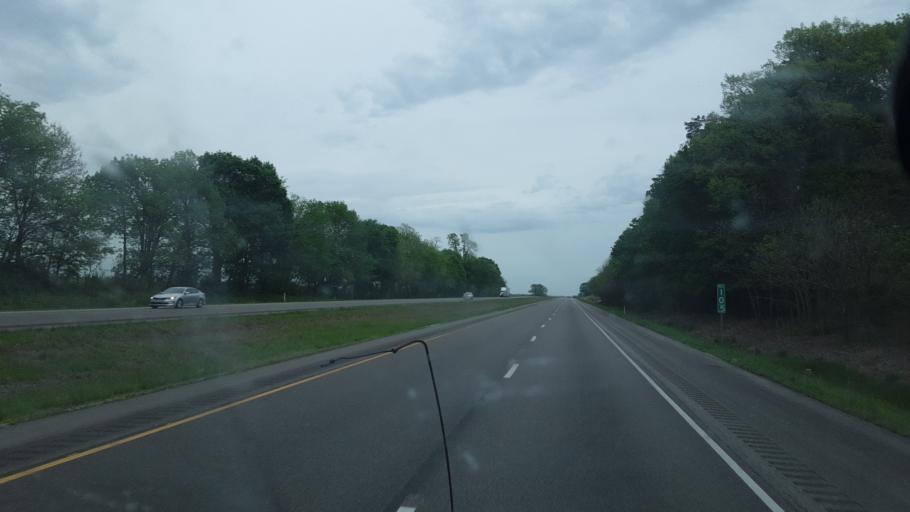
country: US
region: Indiana
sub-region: Posey County
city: Poseyville
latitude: 38.1842
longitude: -87.8060
